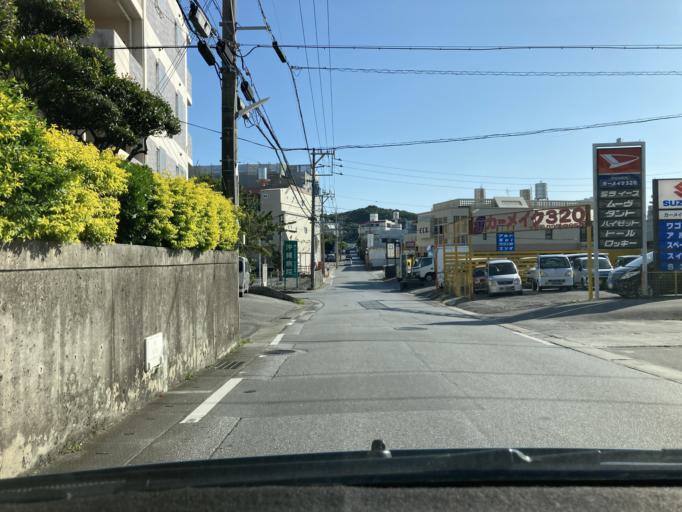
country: JP
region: Okinawa
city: Ginowan
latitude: 26.2533
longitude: 127.7538
